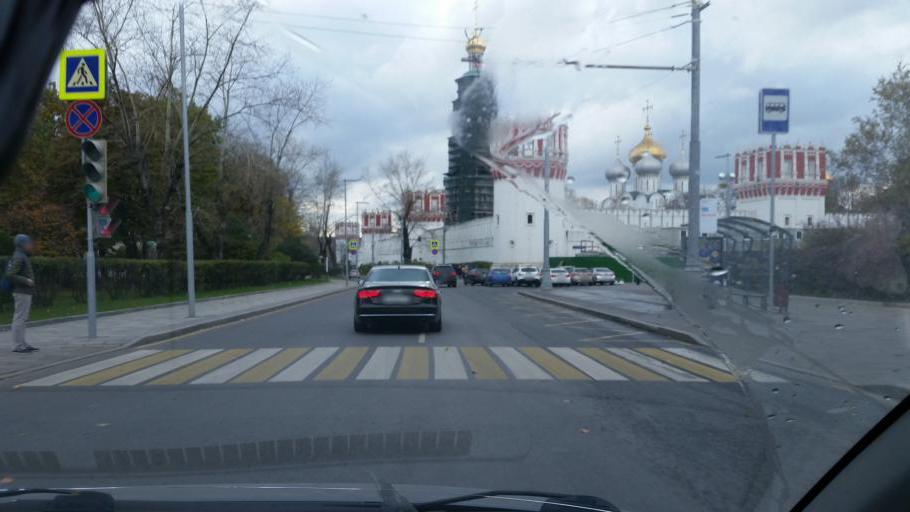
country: RU
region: Moscow
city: Luzhniki
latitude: 55.7270
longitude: 37.5599
